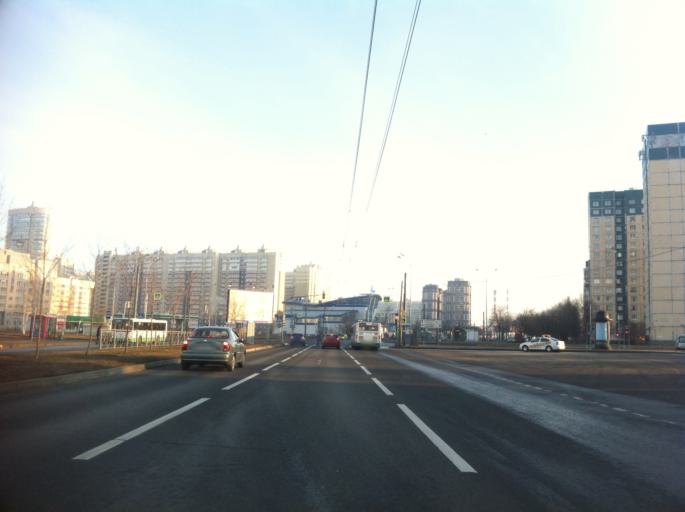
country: RU
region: St.-Petersburg
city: Uritsk
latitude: 59.8564
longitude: 30.1763
